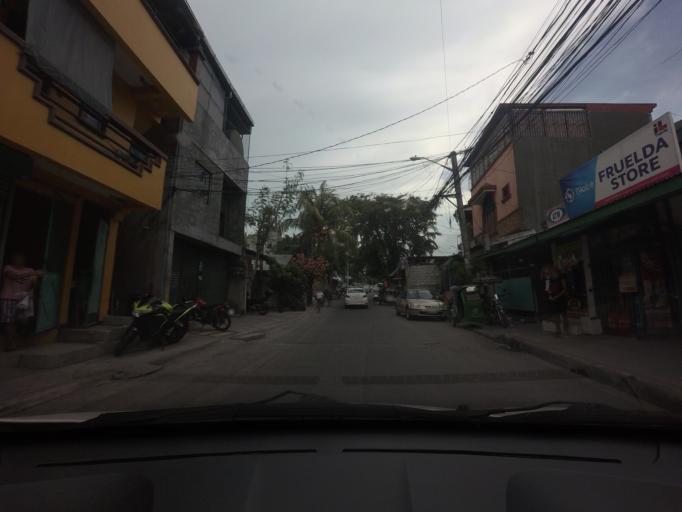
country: PH
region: Calabarzon
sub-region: Province of Rizal
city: Taguig
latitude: 14.5042
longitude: 121.0539
